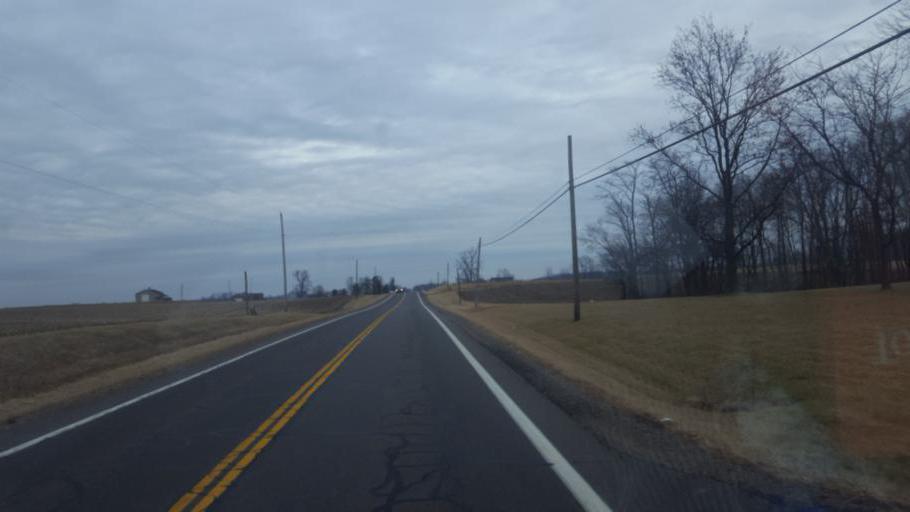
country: US
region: Ohio
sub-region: Morrow County
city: Mount Gilead
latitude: 40.5958
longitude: -82.8237
